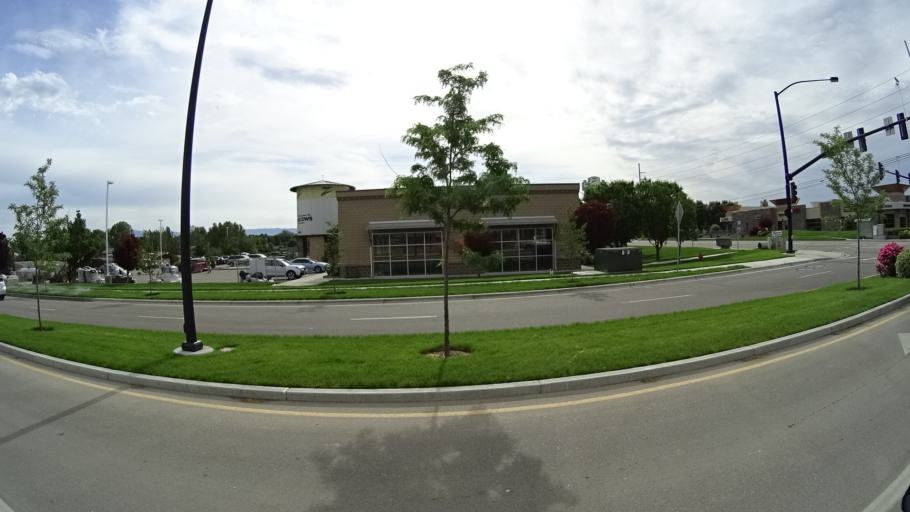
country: US
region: Idaho
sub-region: Ada County
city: Meridian
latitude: 43.5907
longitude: -116.3499
